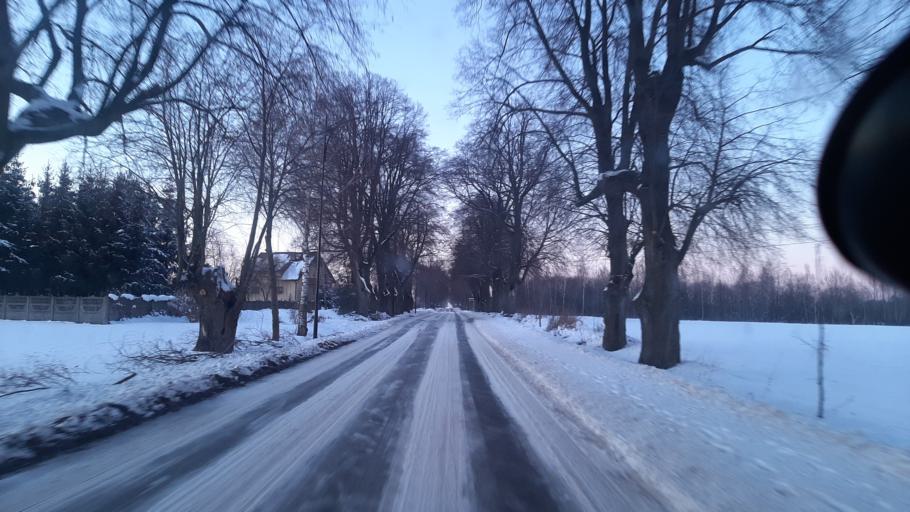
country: PL
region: Lublin Voivodeship
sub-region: Powiat lubelski
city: Lublin
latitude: 51.3291
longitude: 22.5572
